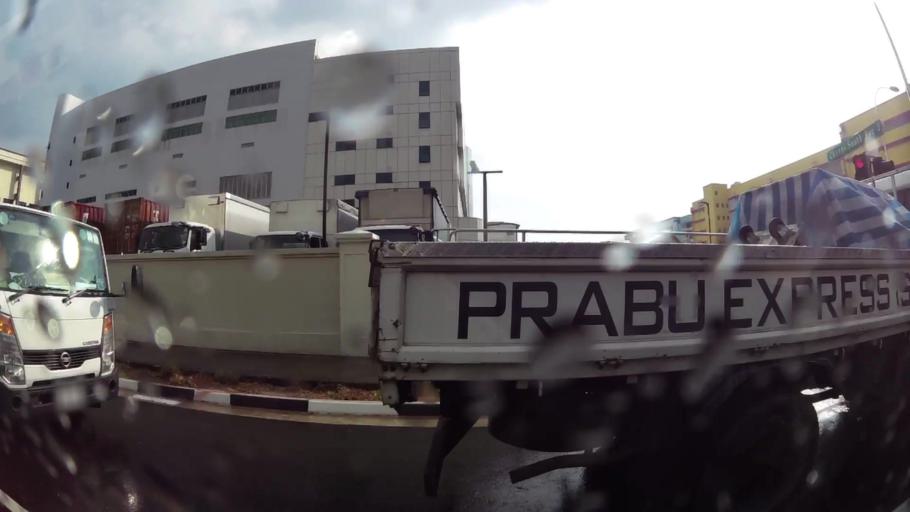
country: SG
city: Singapore
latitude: 1.3316
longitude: 103.9663
